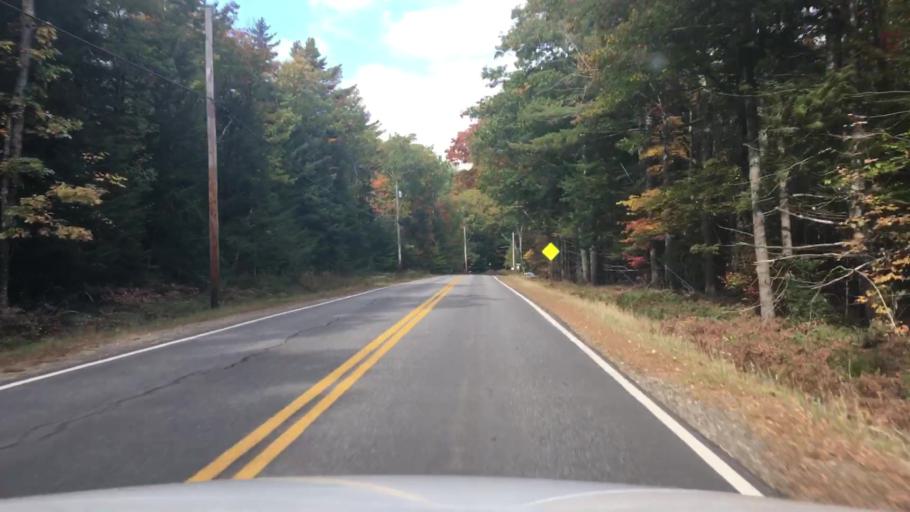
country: US
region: Maine
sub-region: Knox County
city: Hope
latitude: 44.2494
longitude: -69.1270
